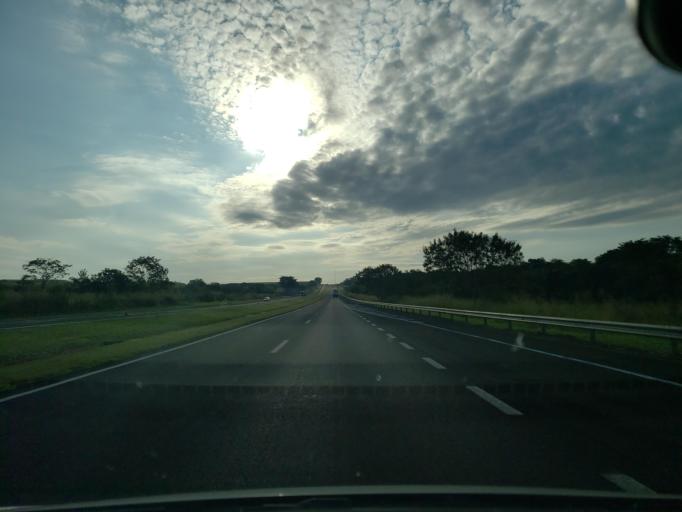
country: BR
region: Sao Paulo
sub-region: Valparaiso
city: Valparaiso
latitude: -21.1662
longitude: -50.9389
